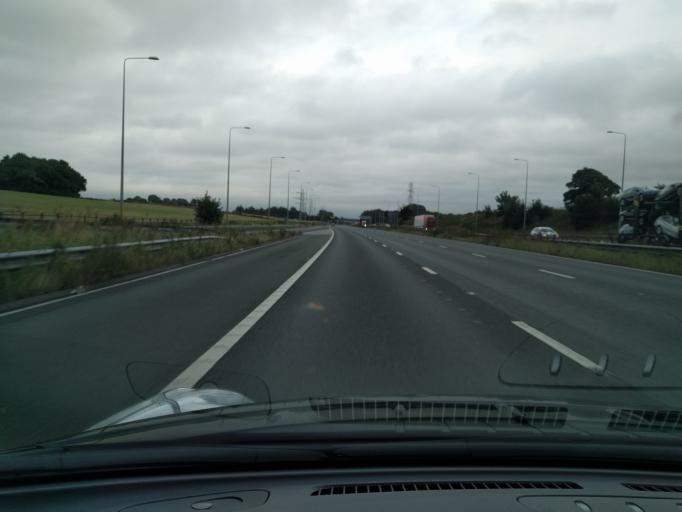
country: GB
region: England
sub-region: Warrington
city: Winwick
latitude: 53.4384
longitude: -2.5807
